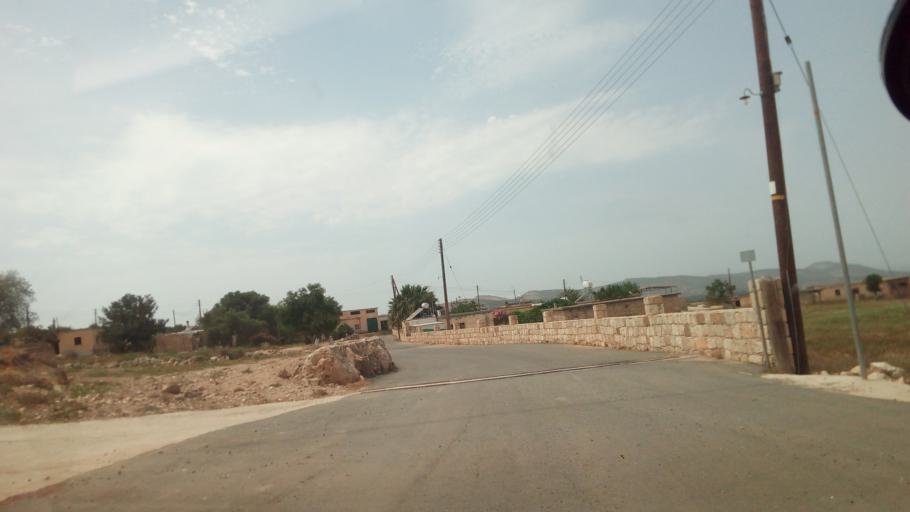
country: CY
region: Pafos
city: Polis
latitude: 34.9983
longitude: 32.3831
